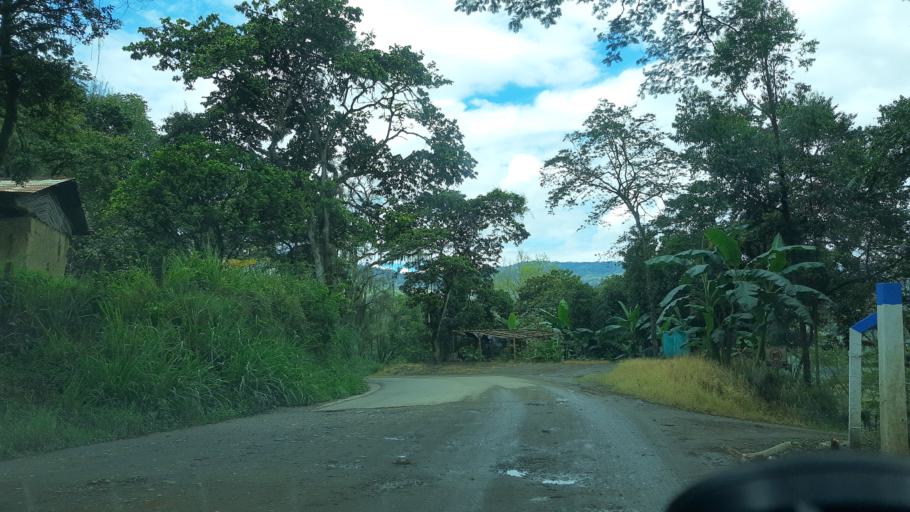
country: CO
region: Boyaca
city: Garagoa
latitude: 5.0697
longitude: -73.3811
